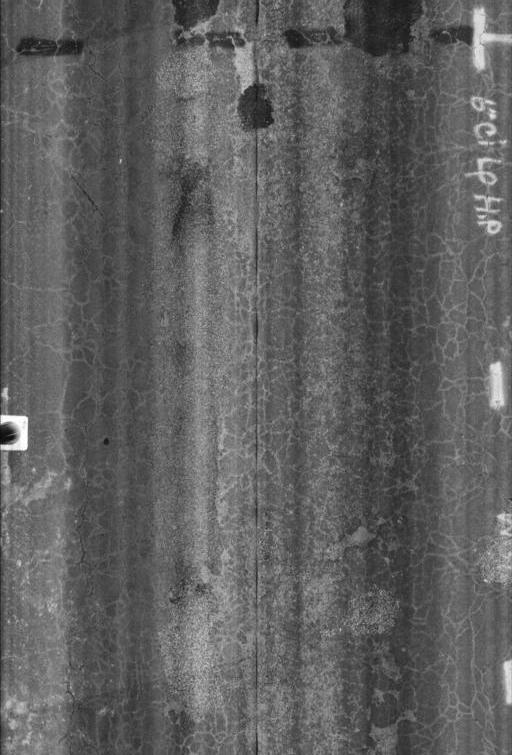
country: US
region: Maryland
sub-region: Montgomery County
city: Friendship Village
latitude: 38.9456
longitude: -77.0871
